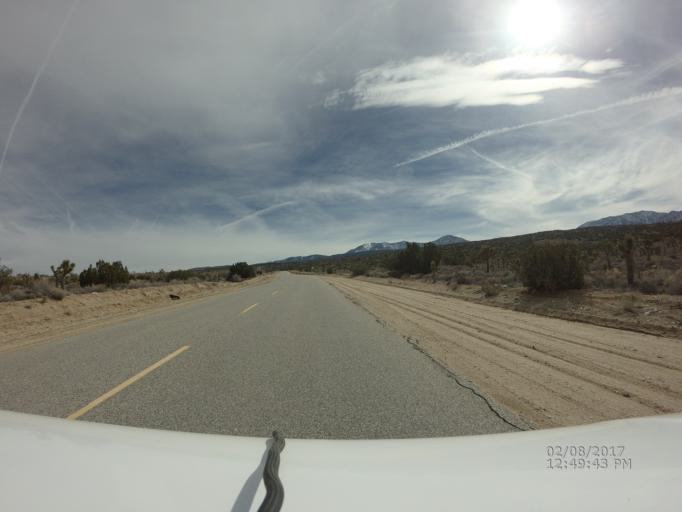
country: US
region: California
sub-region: Los Angeles County
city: Lake Los Angeles
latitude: 34.4692
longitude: -117.8275
